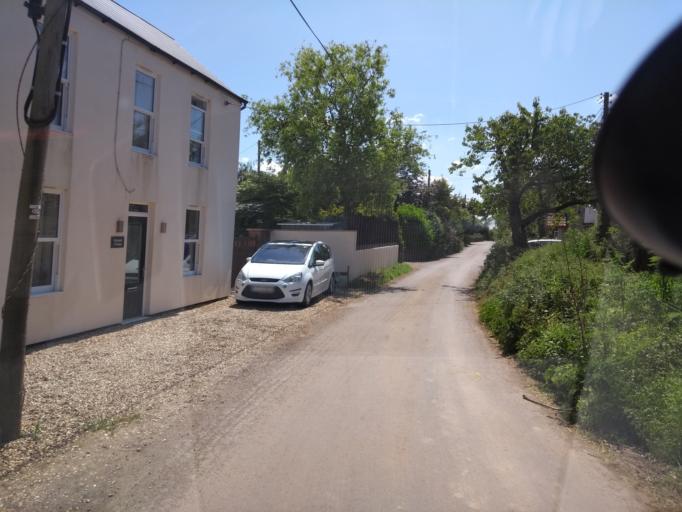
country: GB
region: England
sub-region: Somerset
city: North Petherton
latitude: 51.0593
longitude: -3.0006
